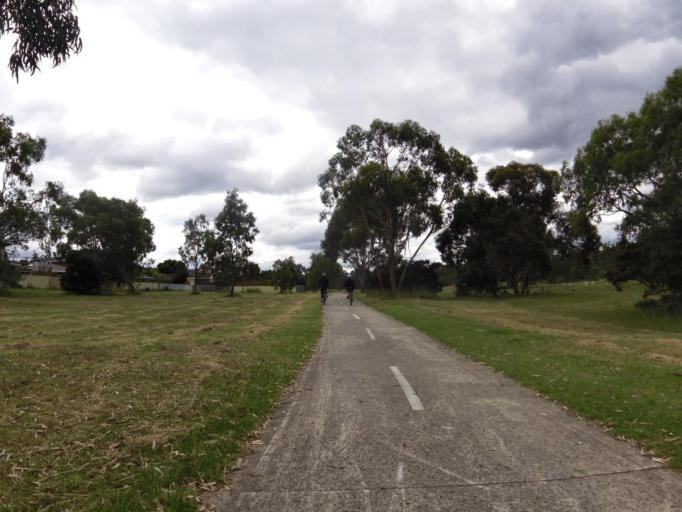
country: AU
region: Victoria
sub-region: Darebin
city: Kingsbury
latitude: -37.7056
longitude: 145.0338
